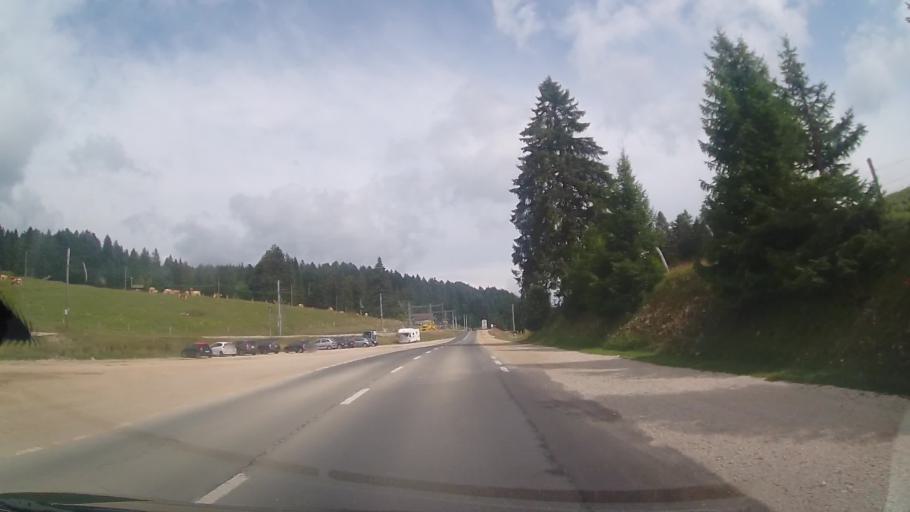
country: CH
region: Vaud
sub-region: Nyon District
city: Saint-Cergue
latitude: 46.4544
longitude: 6.1085
